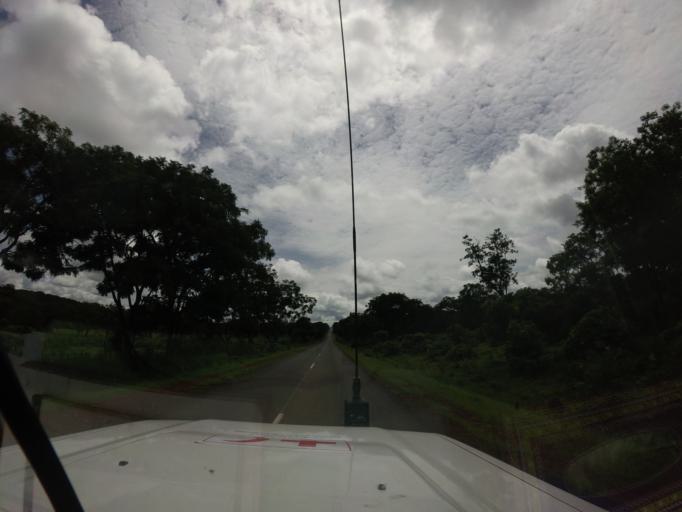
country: SL
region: Northern Province
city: Gberia Fotombu
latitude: 10.0938
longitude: -11.1409
